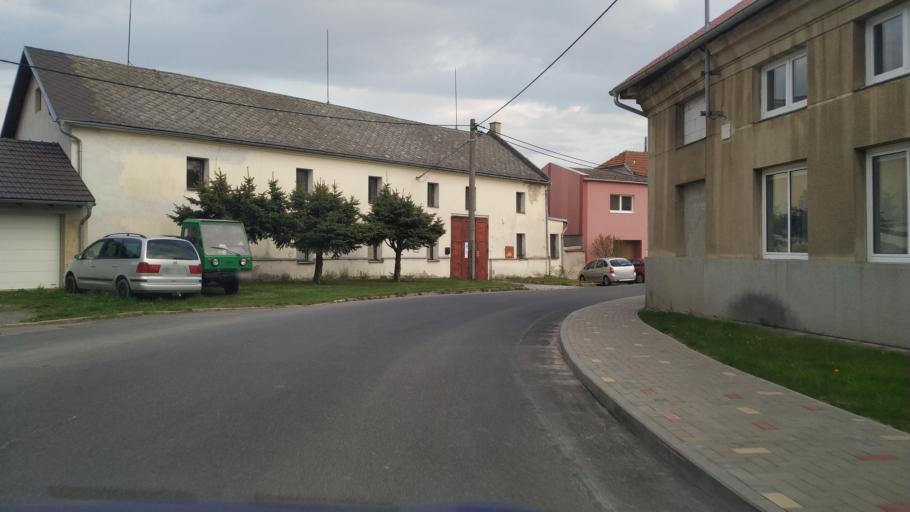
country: CZ
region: Olomoucky
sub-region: Okres Olomouc
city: Slatinice
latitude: 49.5488
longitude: 17.0938
